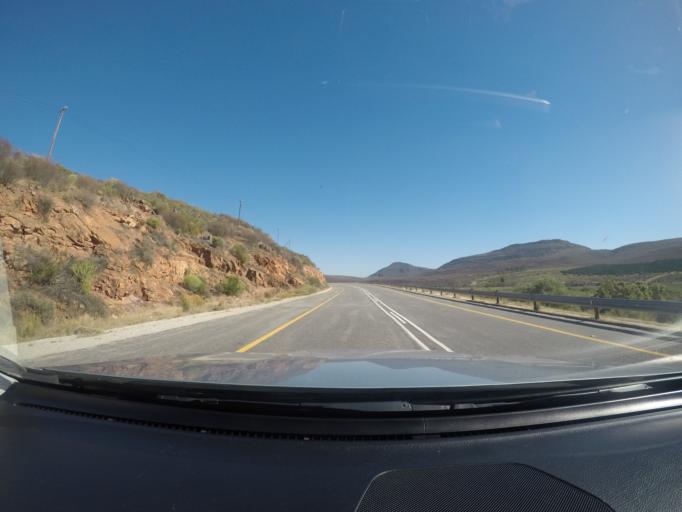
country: ZA
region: Western Cape
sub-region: West Coast District Municipality
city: Clanwilliam
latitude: -32.3946
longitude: 18.9500
